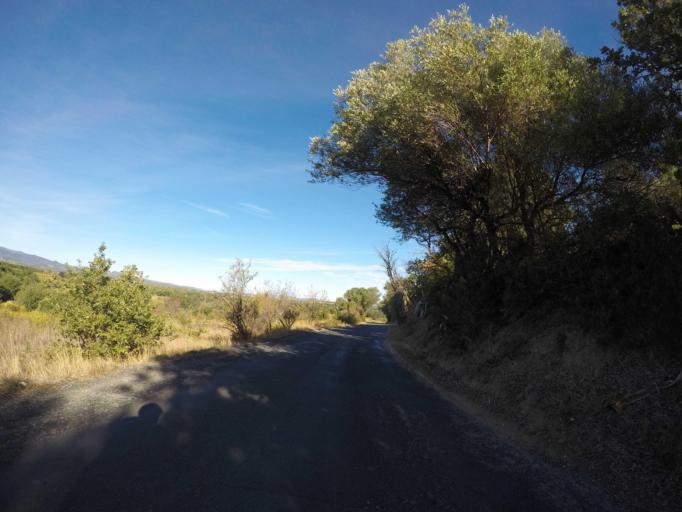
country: FR
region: Languedoc-Roussillon
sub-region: Departement des Pyrenees-Orientales
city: Trouillas
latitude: 42.5821
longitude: 2.8103
